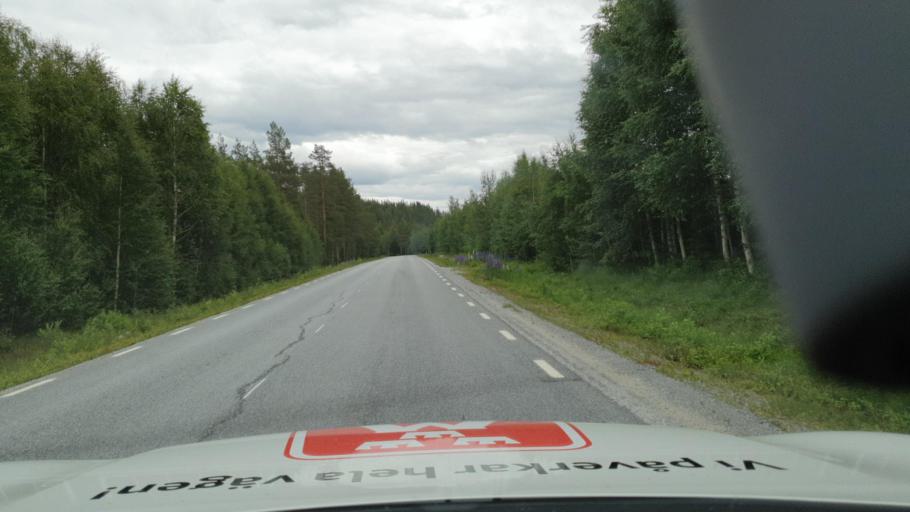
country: SE
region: Vaesterbotten
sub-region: Bjurholms Kommun
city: Bjurholm
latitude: 63.8790
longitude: 19.0045
